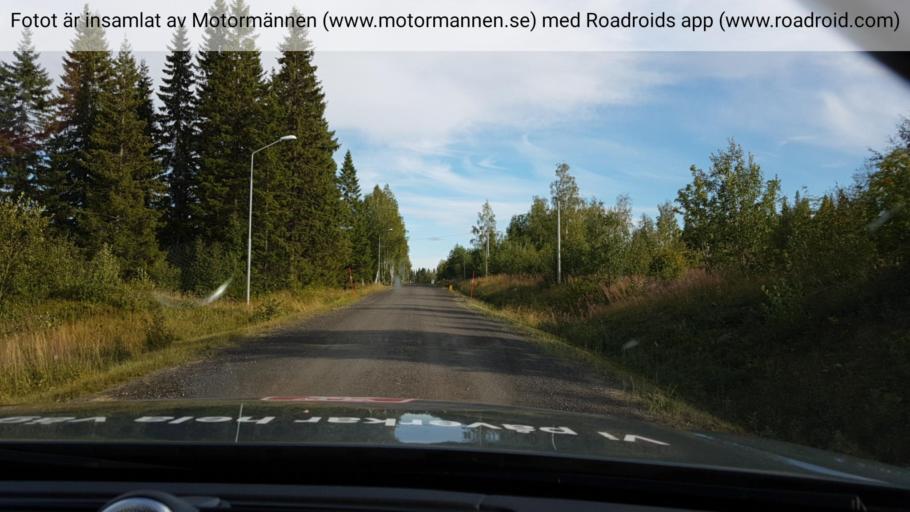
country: SE
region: Jaemtland
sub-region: Stroemsunds Kommun
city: Stroemsund
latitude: 64.1259
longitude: 15.7994
